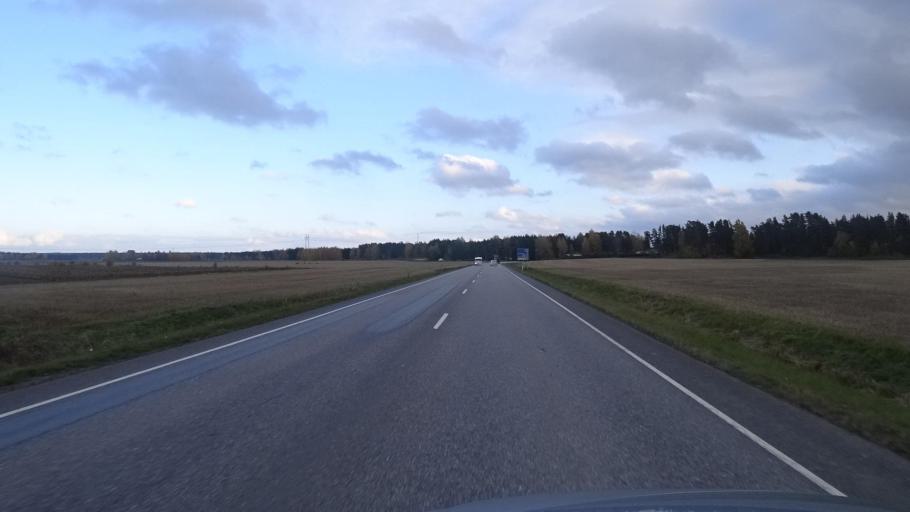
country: FI
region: Satakunta
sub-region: Rauma
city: Saekylae
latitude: 61.0411
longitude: 22.3786
